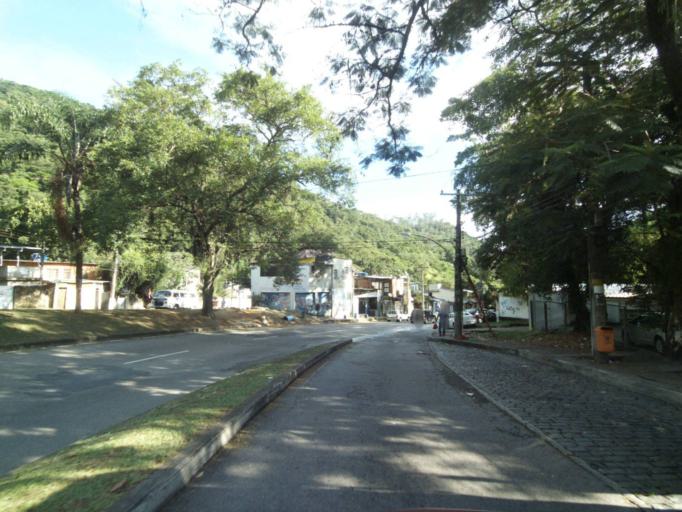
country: BR
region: Rio de Janeiro
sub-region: Rio De Janeiro
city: Rio de Janeiro
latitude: -22.9256
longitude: -43.3151
